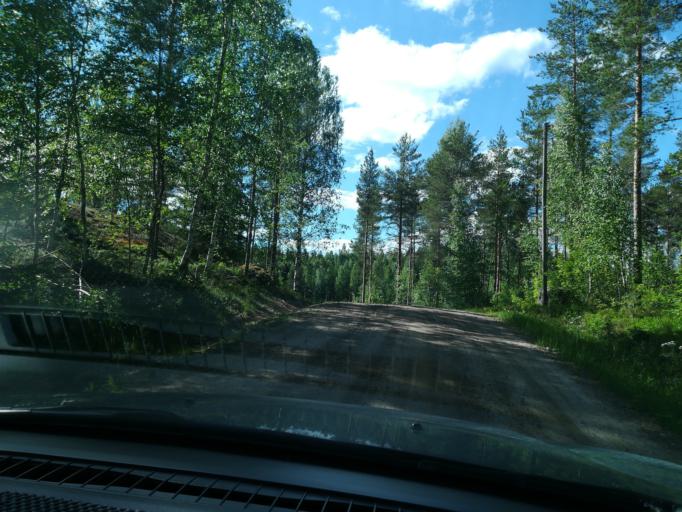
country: FI
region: Southern Savonia
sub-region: Mikkeli
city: Puumala
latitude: 61.6641
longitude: 28.1471
